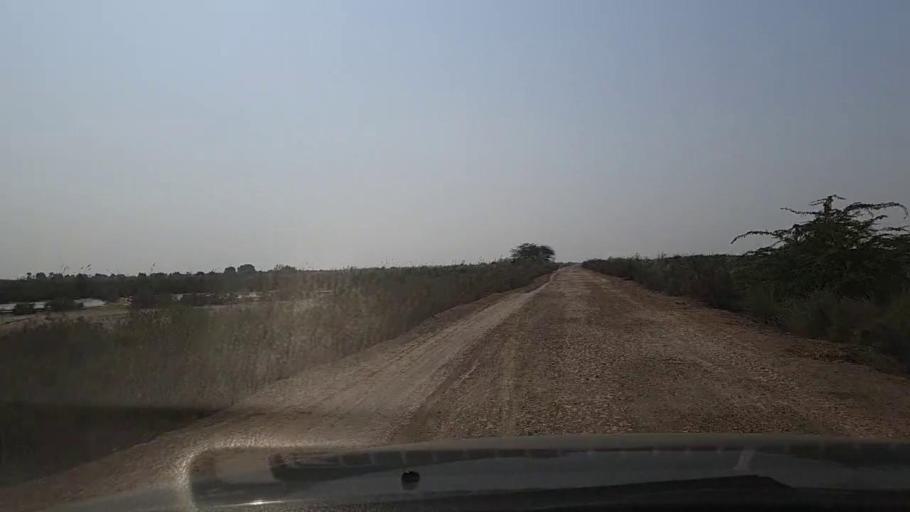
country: PK
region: Sindh
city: Mirpur Sakro
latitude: 24.3807
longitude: 67.6607
